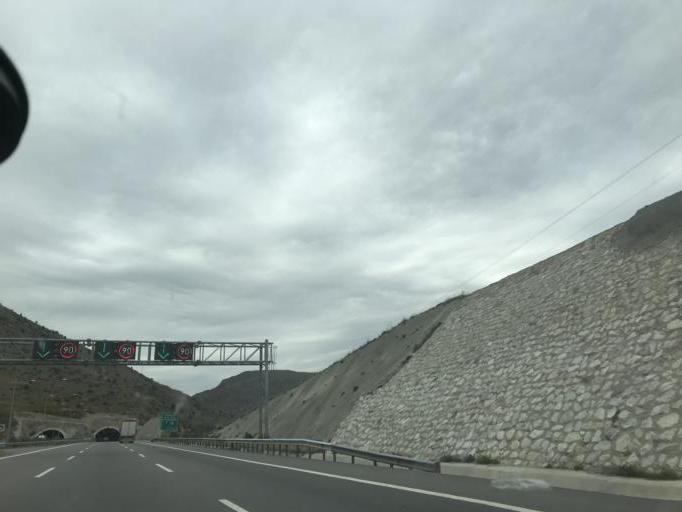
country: TR
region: Nigde
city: Ciftehan
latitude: 37.5712
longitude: 34.7540
